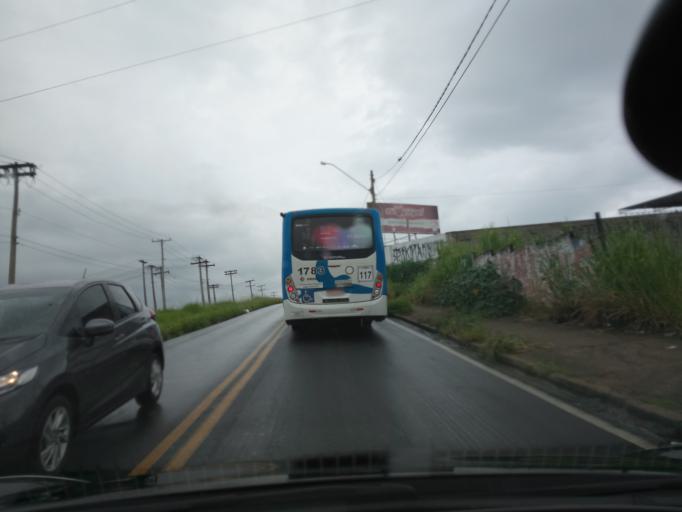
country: BR
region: Sao Paulo
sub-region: Campinas
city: Campinas
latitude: -22.9779
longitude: -47.1043
